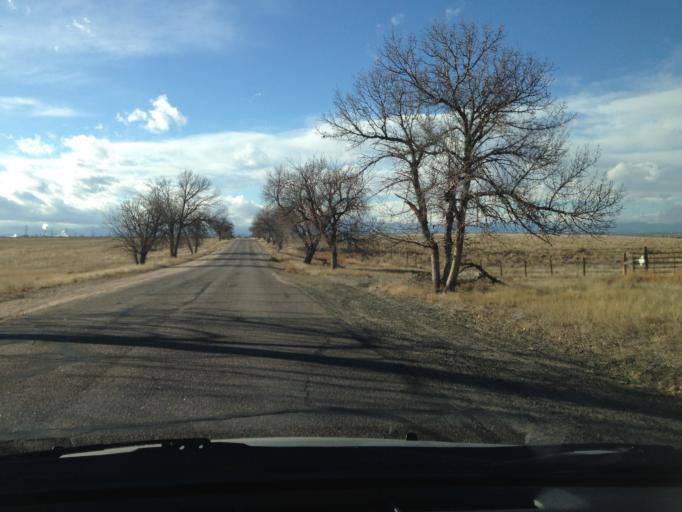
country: US
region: Colorado
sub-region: Adams County
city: Derby
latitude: 39.8273
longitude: -104.8793
